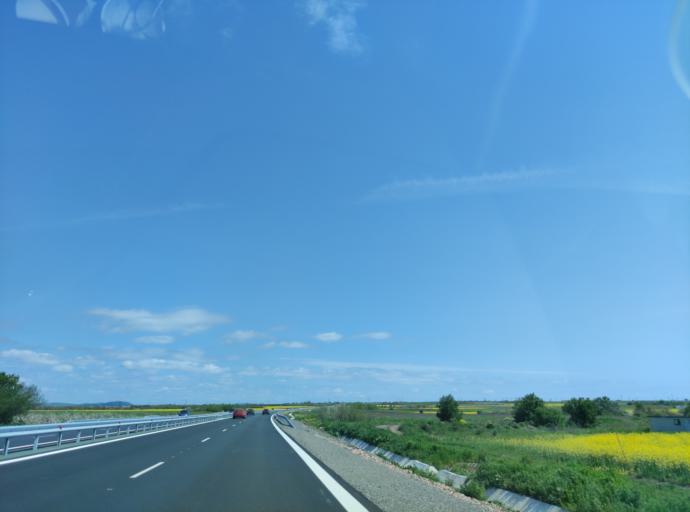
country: BG
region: Burgas
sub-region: Obshtina Pomorie
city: Pomorie
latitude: 42.5698
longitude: 27.5736
